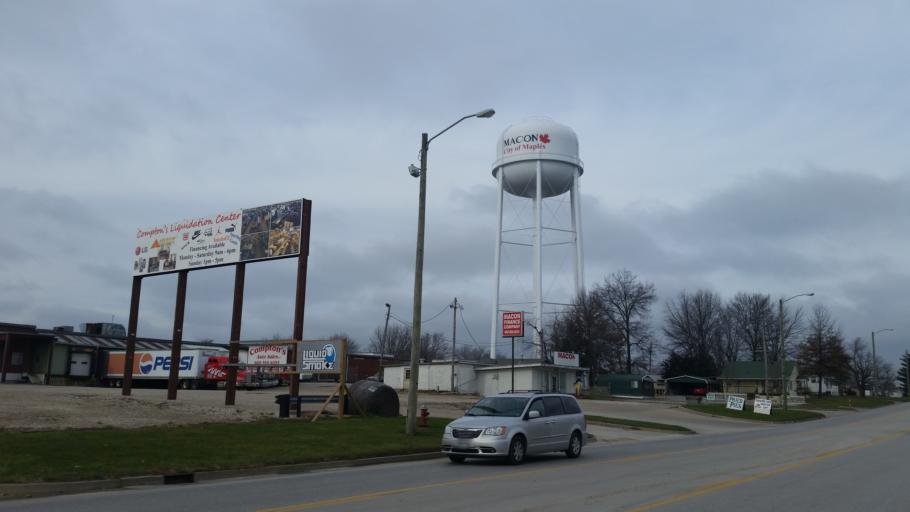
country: US
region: Missouri
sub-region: Macon County
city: Macon
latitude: 39.7296
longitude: -92.4658
